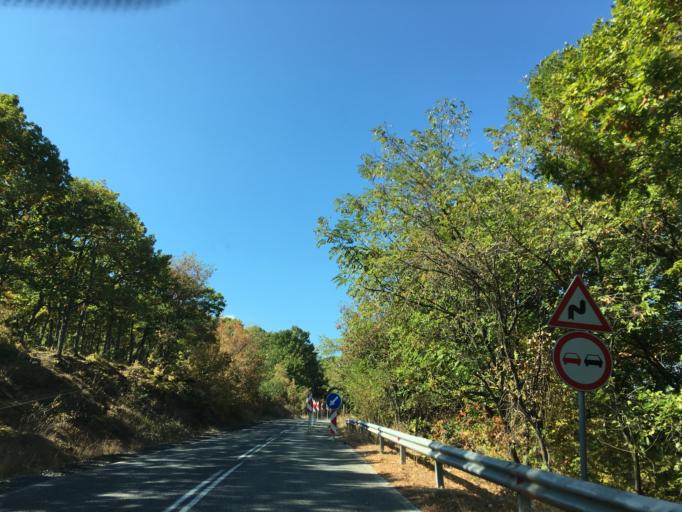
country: BG
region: Kurdzhali
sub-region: Obshtina Krumovgrad
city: Krumovgrad
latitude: 41.4732
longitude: 25.5424
